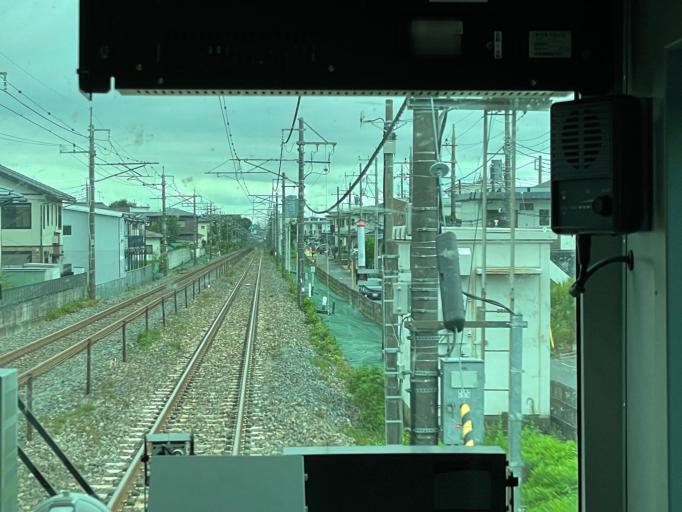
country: JP
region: Tochigi
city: Utsunomiya-shi
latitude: 36.5842
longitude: 139.9237
